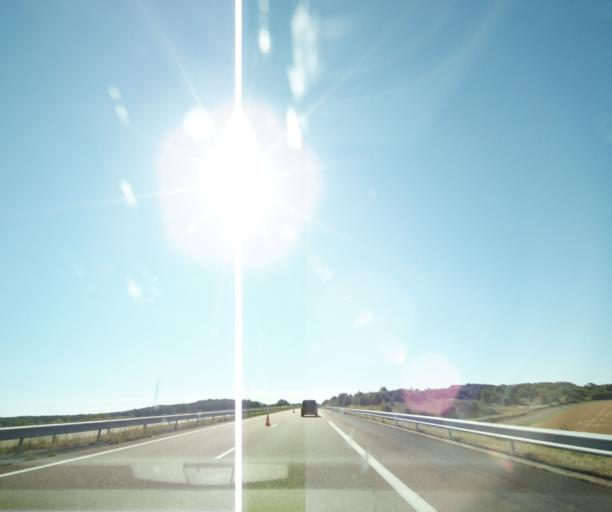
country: FR
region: Champagne-Ardenne
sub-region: Departement de l'Aube
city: Ville-sous-la-Ferte
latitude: 48.1286
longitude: 4.6844
